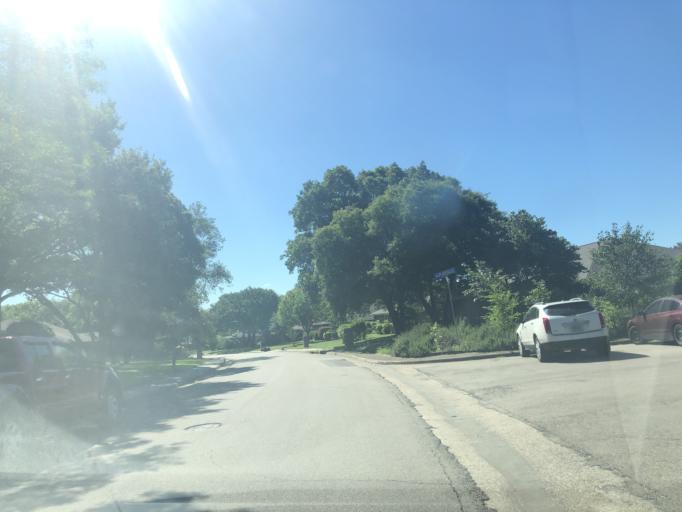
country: US
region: Texas
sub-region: Dallas County
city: Duncanville
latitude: 32.6507
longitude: -96.9327
